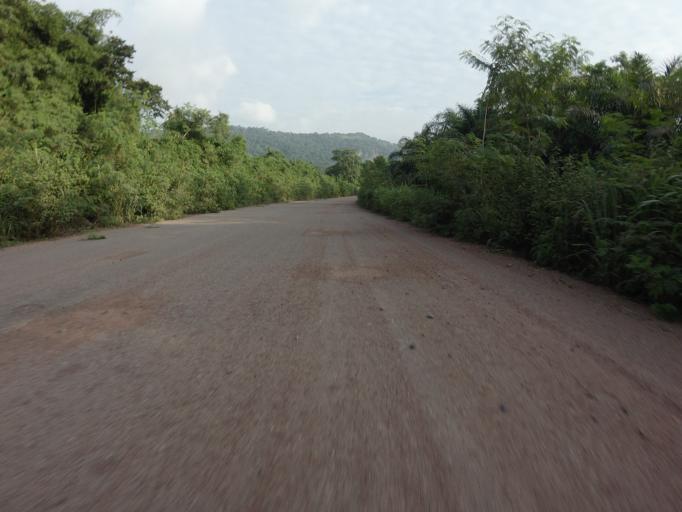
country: TG
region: Plateaux
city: Kpalime
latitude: 6.9318
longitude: 0.4627
